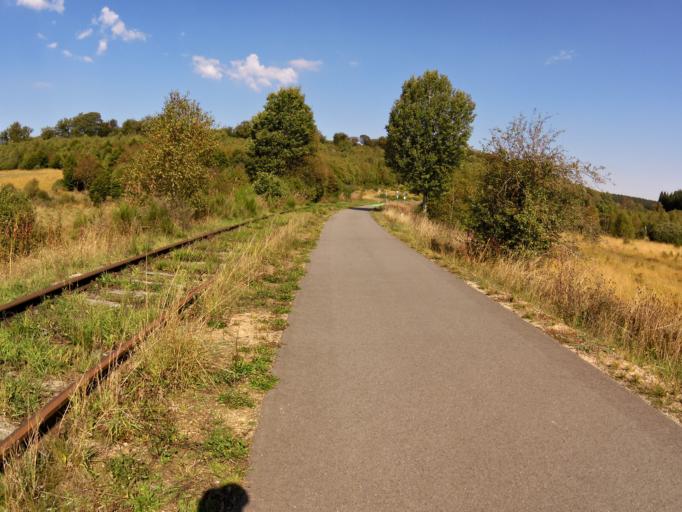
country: BE
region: Wallonia
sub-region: Province de Liege
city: Butgenbach
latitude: 50.4930
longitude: 6.1701
